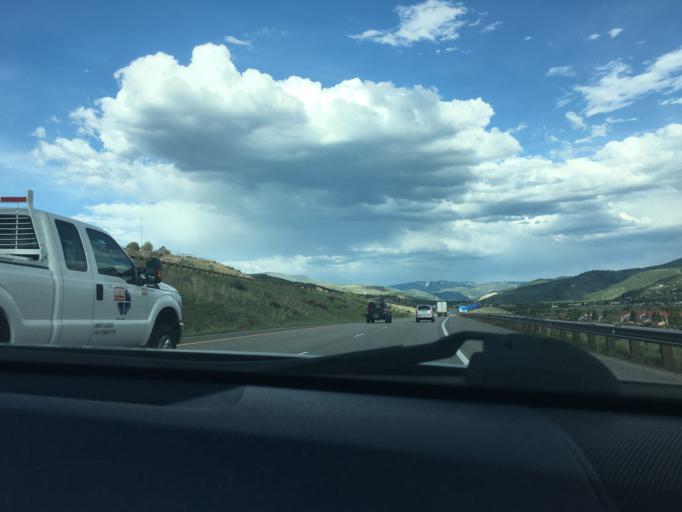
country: US
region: Colorado
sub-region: Eagle County
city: Edwards
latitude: 39.6563
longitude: -106.6210
